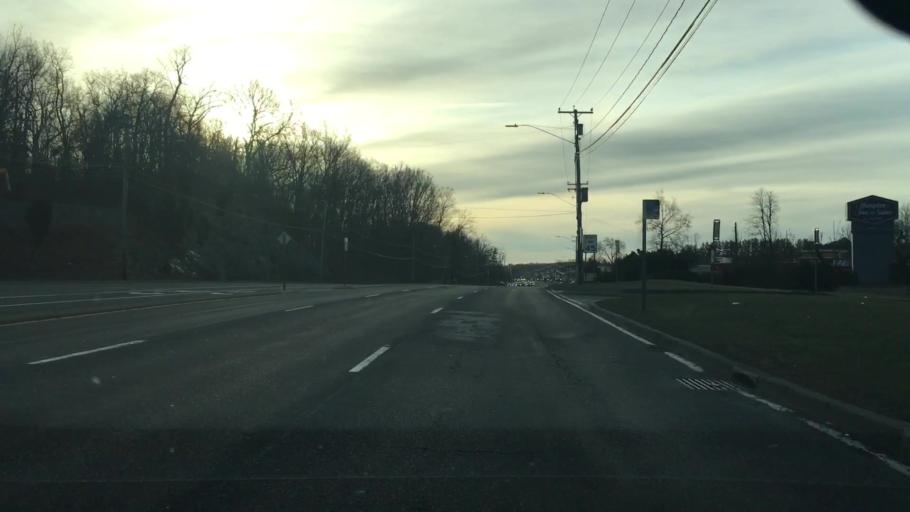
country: US
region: New York
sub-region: Dutchess County
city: Spackenkill
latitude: 41.6508
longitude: -73.9280
